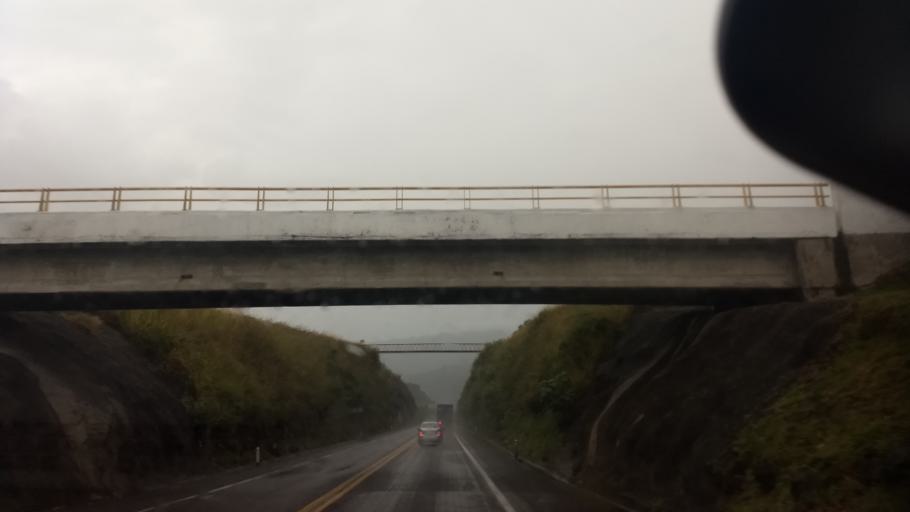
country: MX
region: Jalisco
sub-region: Tonila
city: San Marcos
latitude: 19.4374
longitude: -103.4793
